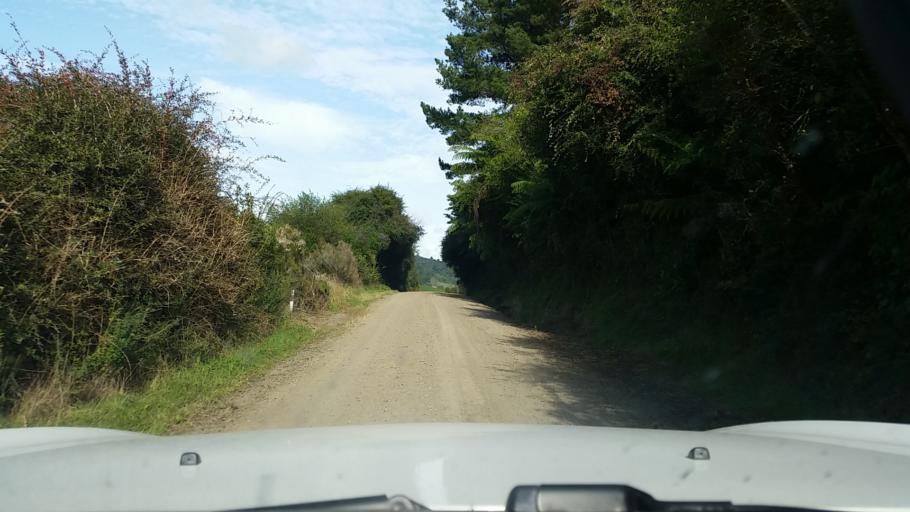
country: NZ
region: Waikato
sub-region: Matamata-Piako District
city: Matamata
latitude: -37.8135
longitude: 175.6345
